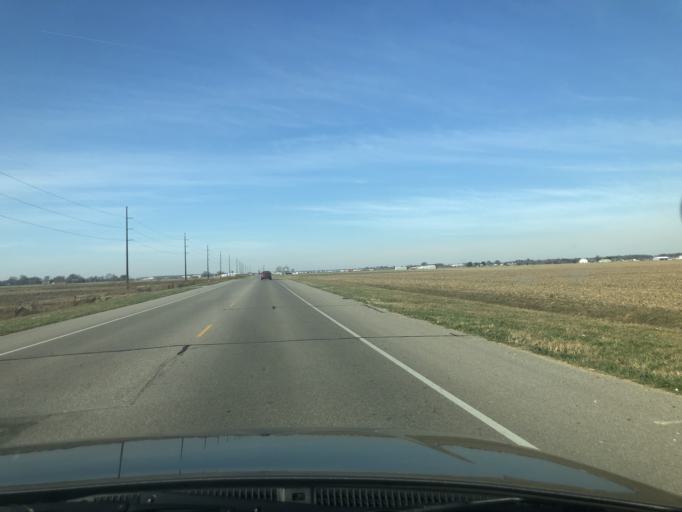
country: US
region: Indiana
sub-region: Warrick County
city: Newburgh
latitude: 37.9914
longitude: -87.4245
